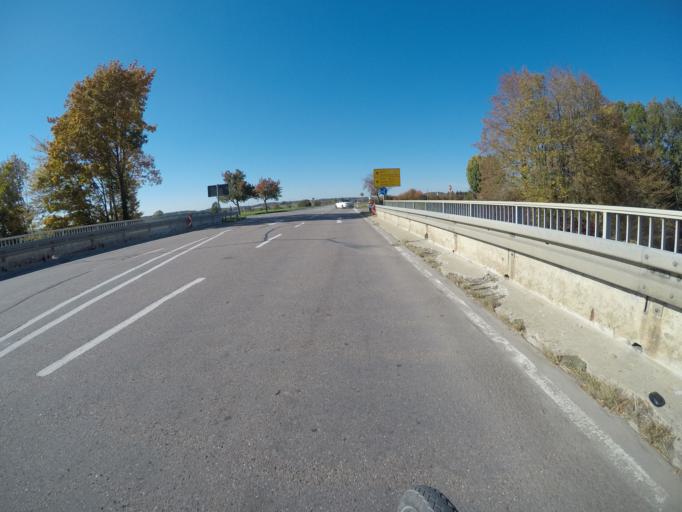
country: DE
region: Baden-Wuerttemberg
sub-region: Regierungsbezirk Stuttgart
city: Bondorf
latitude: 48.5486
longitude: 8.8436
